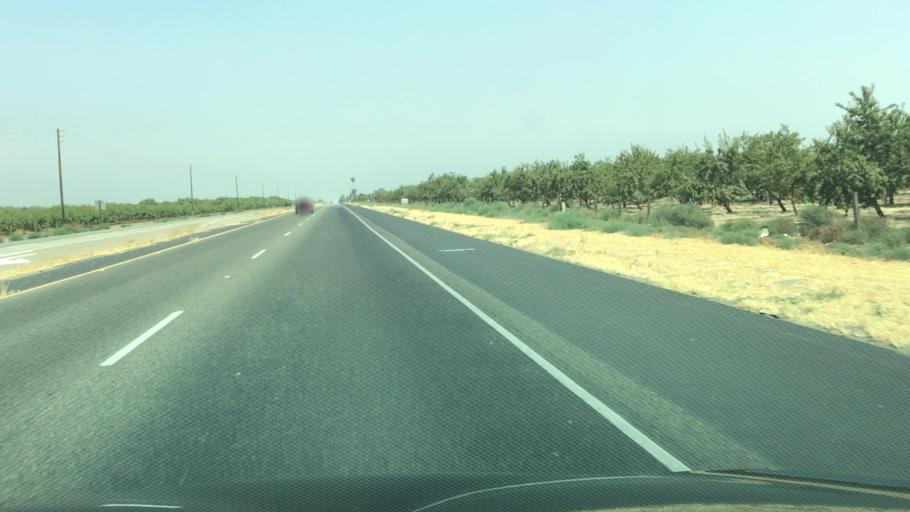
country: US
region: California
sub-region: Merced County
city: Dos Palos
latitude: 37.0835
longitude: -120.4546
